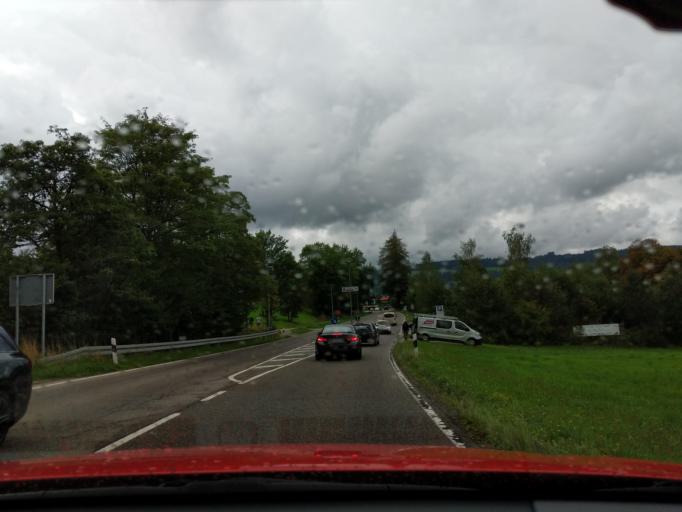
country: DE
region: Bavaria
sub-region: Swabia
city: Immenstadt im Allgau
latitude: 47.5642
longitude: 10.1969
